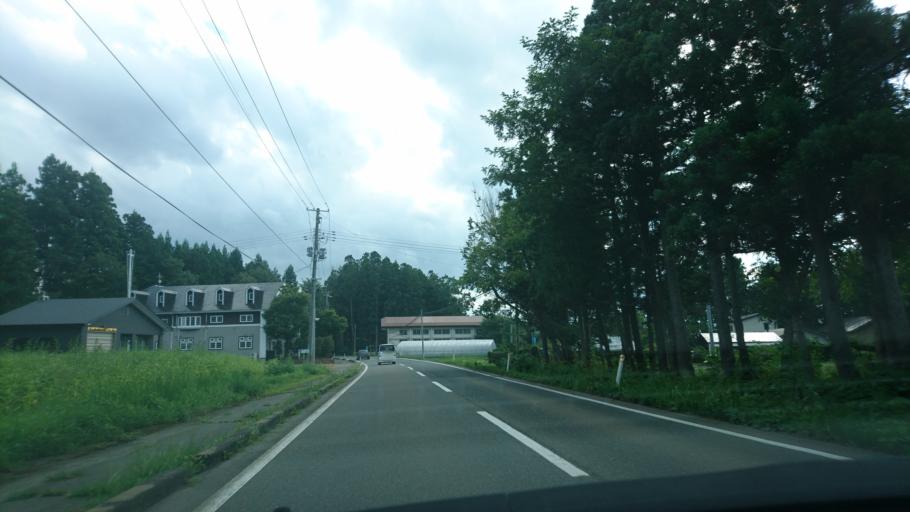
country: JP
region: Iwate
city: Hanamaki
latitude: 39.4107
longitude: 141.1693
